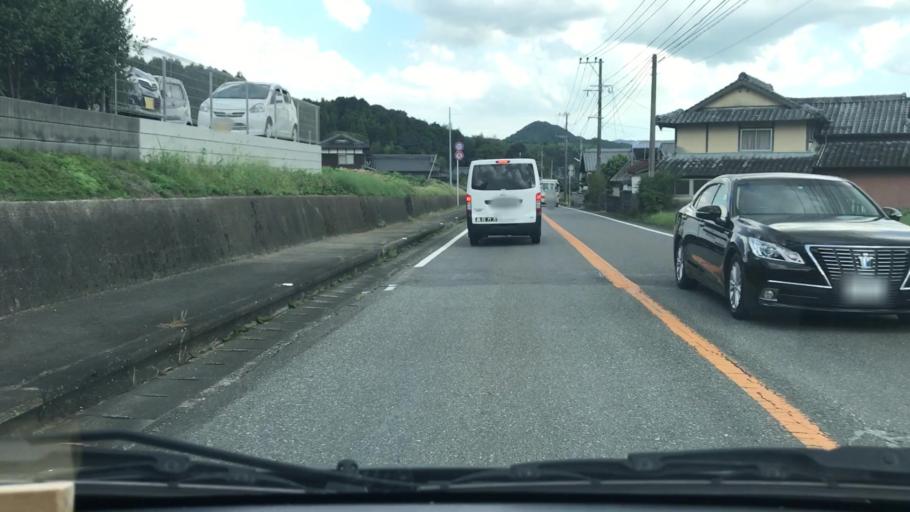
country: JP
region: Saga Prefecture
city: Takeocho-takeo
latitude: 33.2289
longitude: 130.0201
